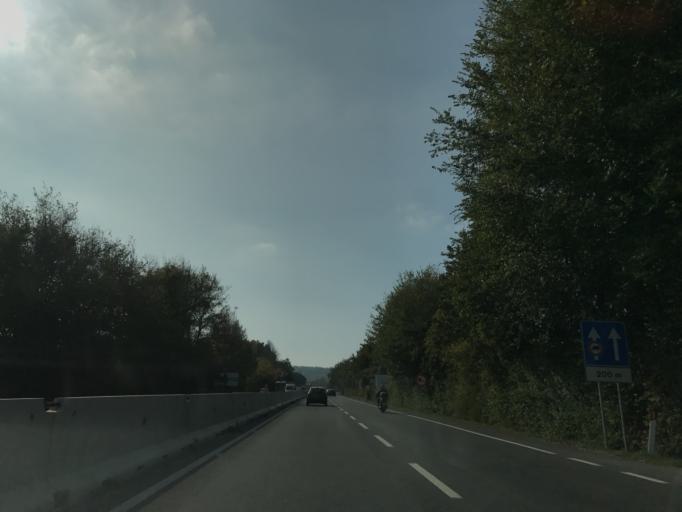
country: IT
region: Emilia-Romagna
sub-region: Provincia di Rimini
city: Cerasolo
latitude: 44.0049
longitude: 12.5439
